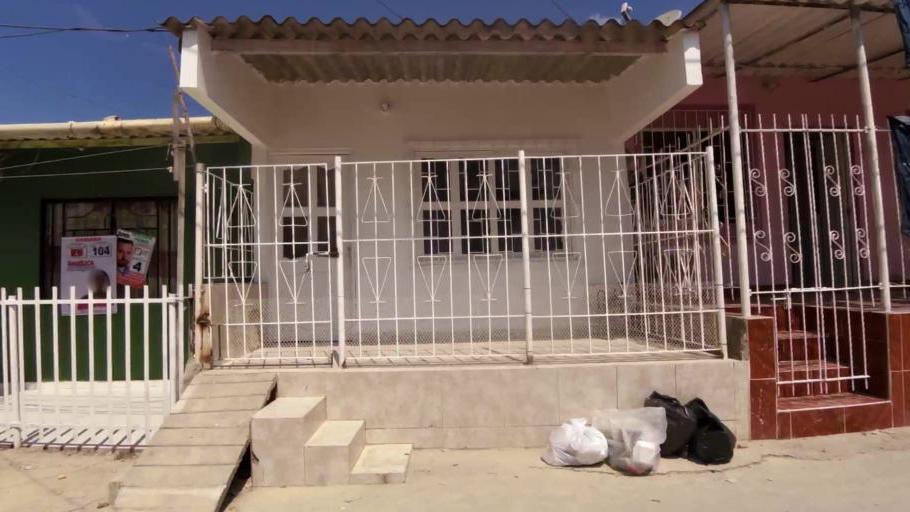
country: CO
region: Bolivar
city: Cartagena
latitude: 10.3457
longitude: -75.4937
